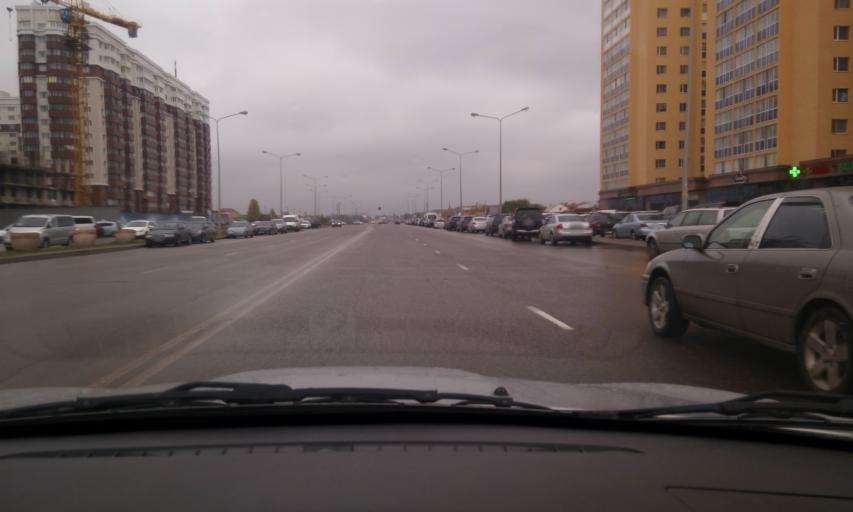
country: KZ
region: Astana Qalasy
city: Astana
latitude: 51.1303
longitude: 71.5015
